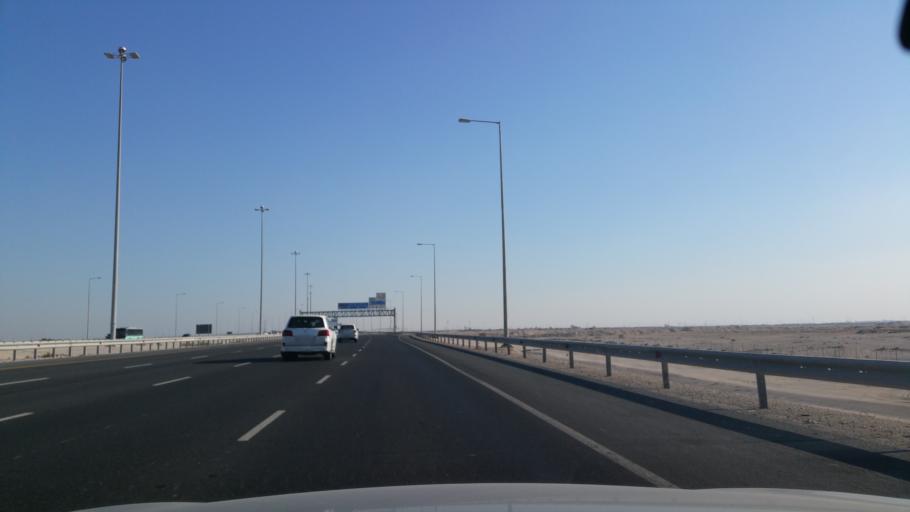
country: QA
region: Al Wakrah
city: Al Wukayr
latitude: 25.1419
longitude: 51.4756
